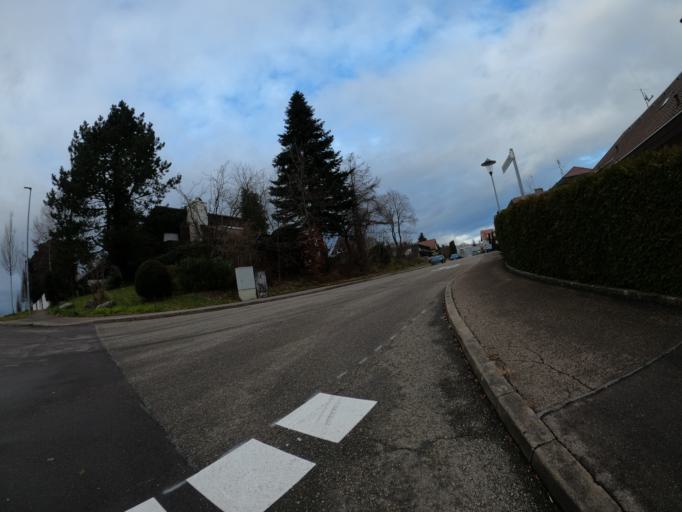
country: DE
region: Baden-Wuerttemberg
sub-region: Regierungsbezirk Stuttgart
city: Waldstetten
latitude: 48.7684
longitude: 9.8320
